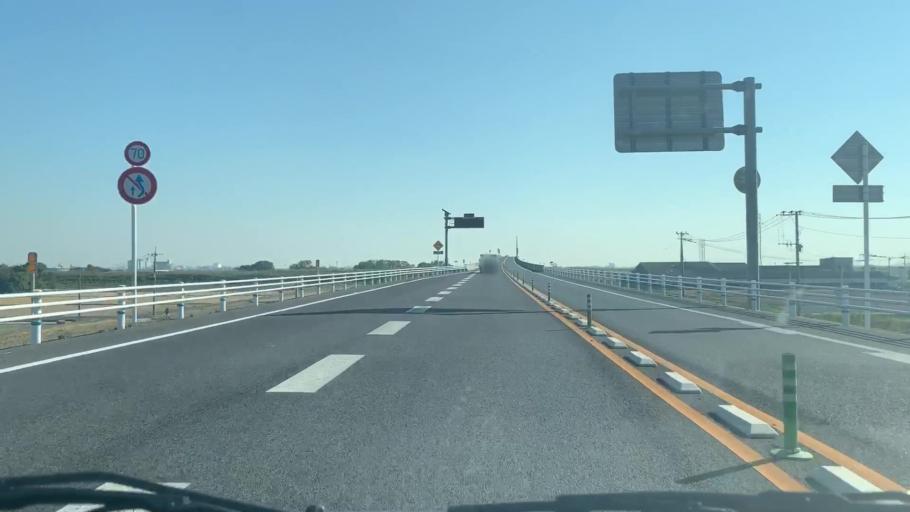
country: JP
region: Saga Prefecture
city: Saga-shi
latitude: 33.2316
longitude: 130.2439
